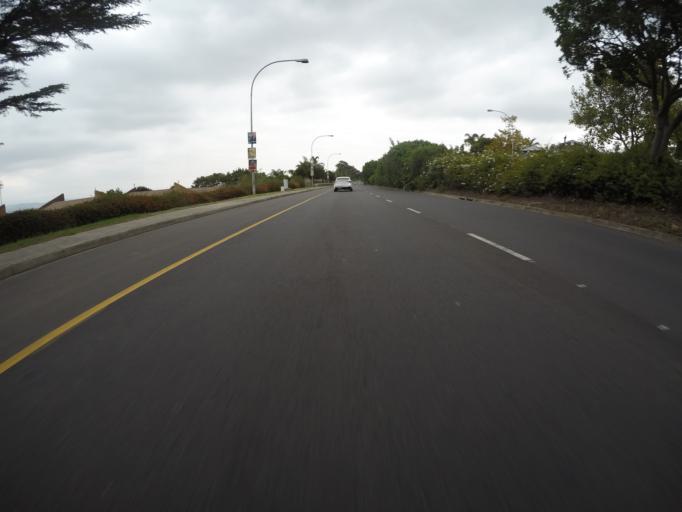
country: ZA
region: Western Cape
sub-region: City of Cape Town
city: Kraaifontein
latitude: -33.8563
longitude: 18.6434
